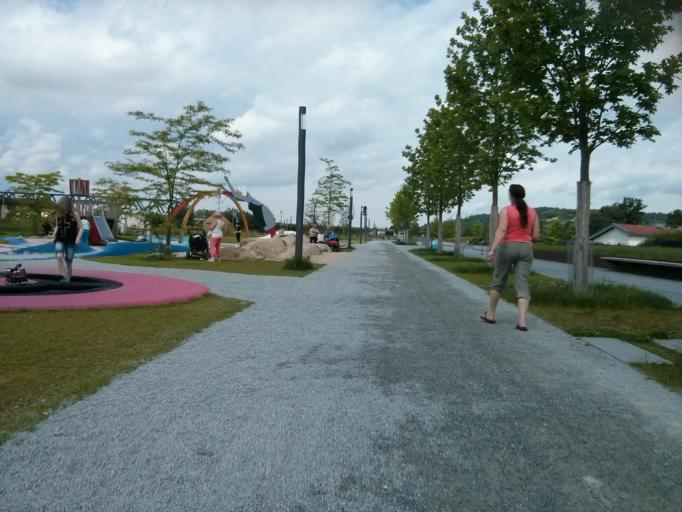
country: DE
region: Bavaria
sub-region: Lower Bavaria
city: Deggendorf
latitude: 48.8306
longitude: 12.9490
